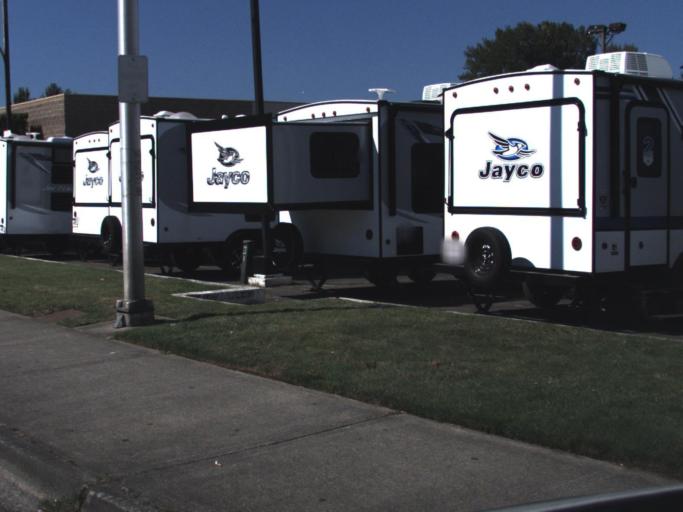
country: US
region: Washington
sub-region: King County
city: Kent
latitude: 47.3857
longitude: -122.2474
